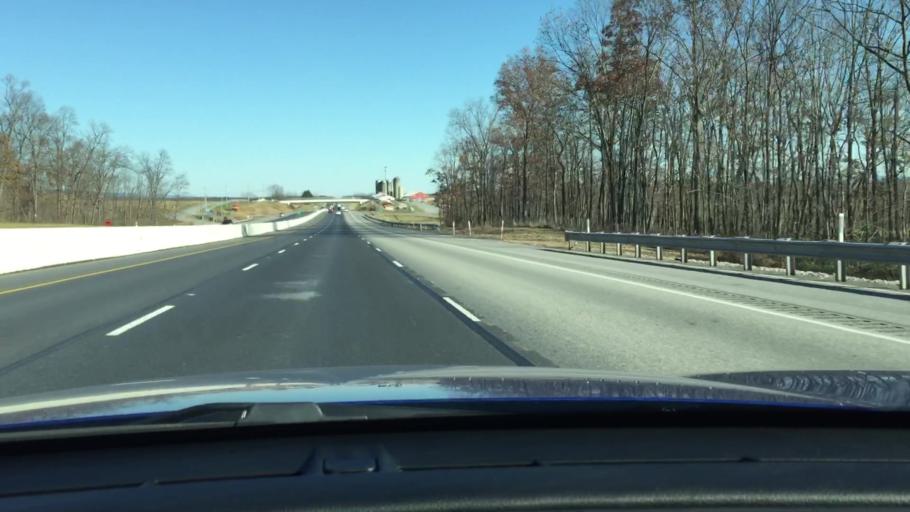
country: US
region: Pennsylvania
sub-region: Cumberland County
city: Shippensburg
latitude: 40.1696
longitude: -77.5707
